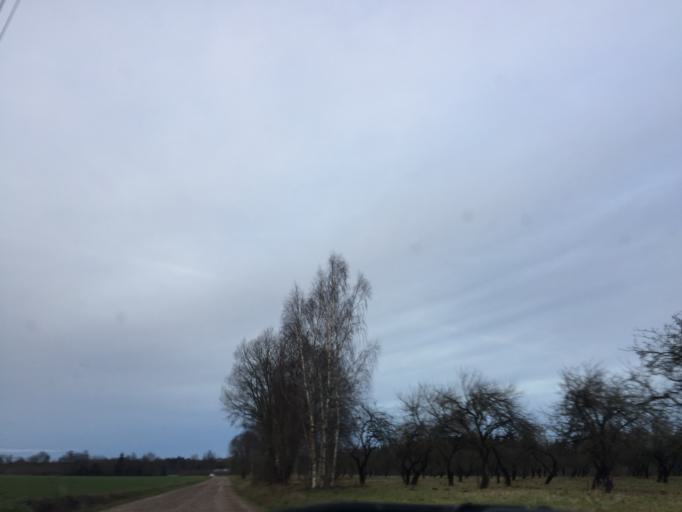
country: LV
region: Limbazu Rajons
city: Limbazi
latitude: 57.5297
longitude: 24.8020
